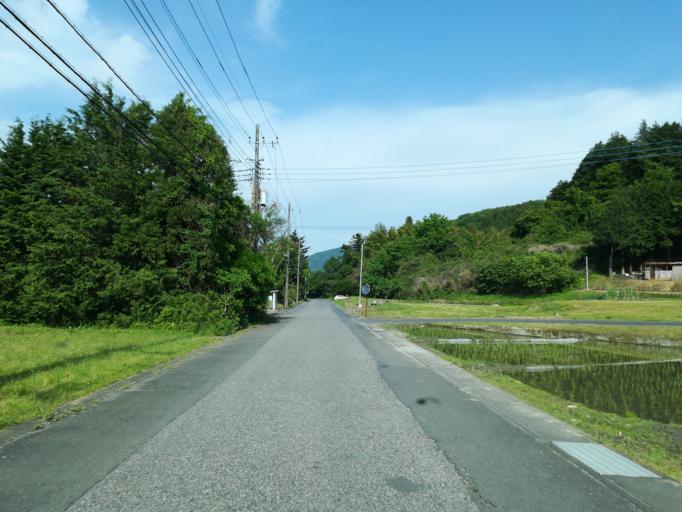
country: JP
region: Ibaraki
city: Tsukuba
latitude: 36.1883
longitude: 140.1548
